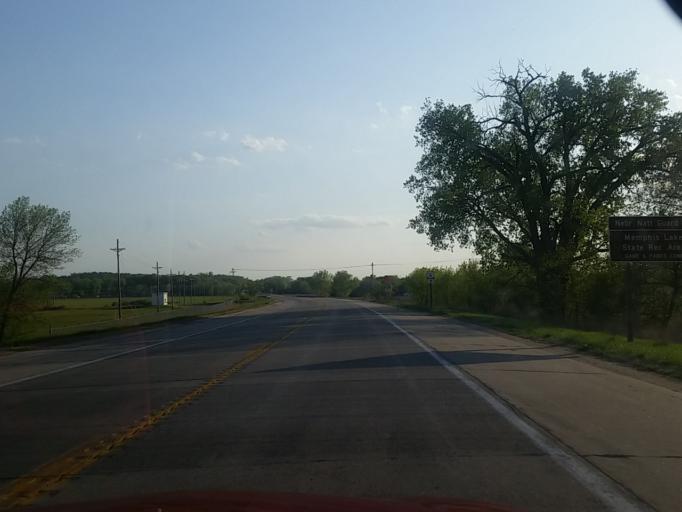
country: US
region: Nebraska
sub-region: Saunders County
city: Ashland
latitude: 41.0588
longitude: -96.3302
